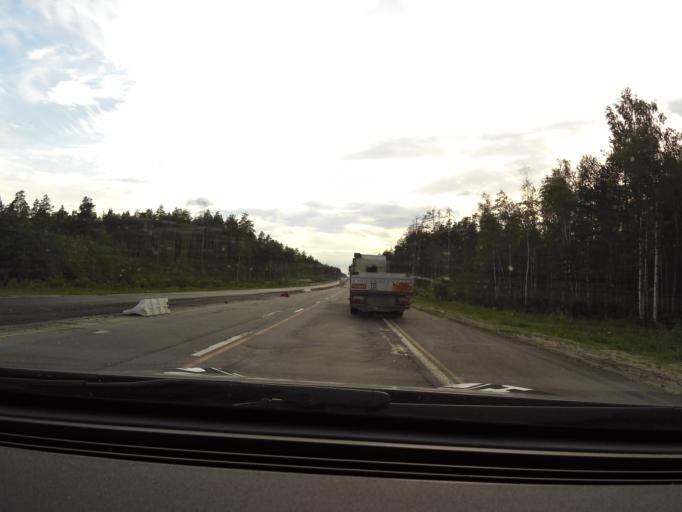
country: RU
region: Vladimir
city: Orgtrud
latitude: 56.1027
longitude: 40.7410
